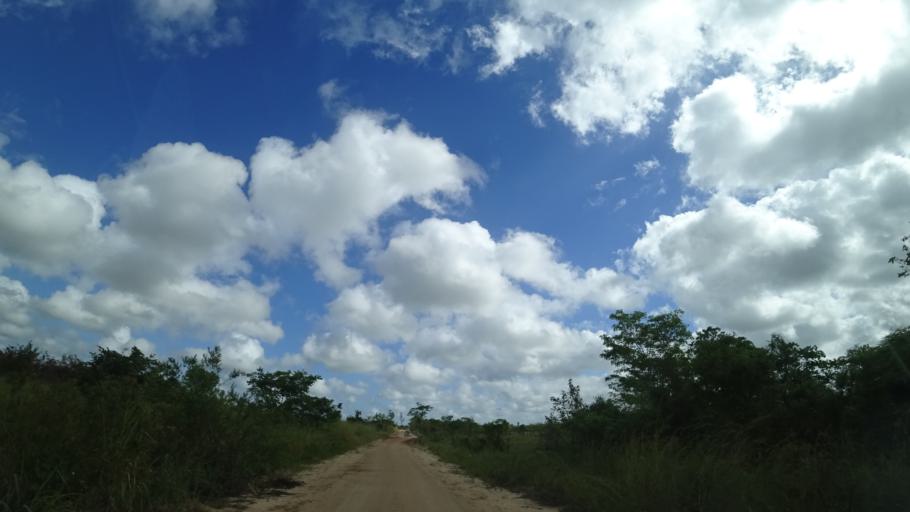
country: MZ
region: Sofala
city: Dondo
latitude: -19.4330
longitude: 34.7115
